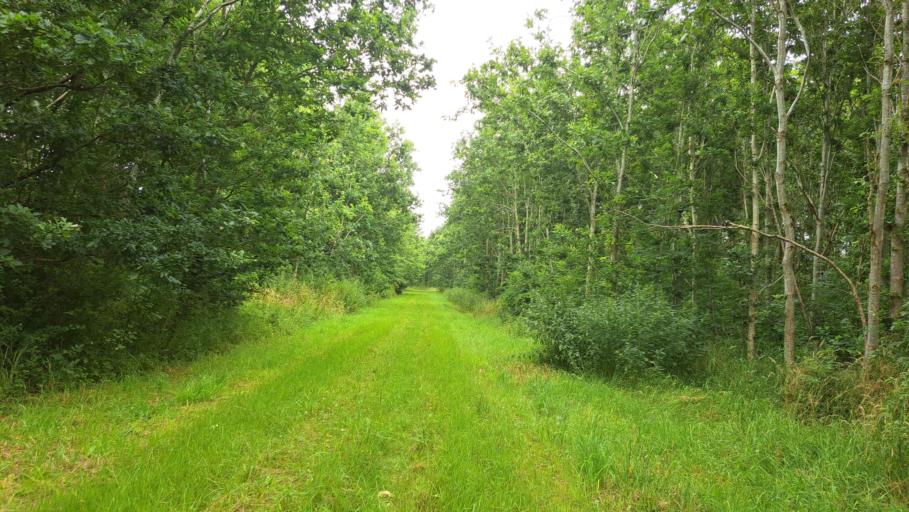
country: DK
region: Central Jutland
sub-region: Hedensted Kommune
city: Hedensted
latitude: 55.8028
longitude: 9.7176
